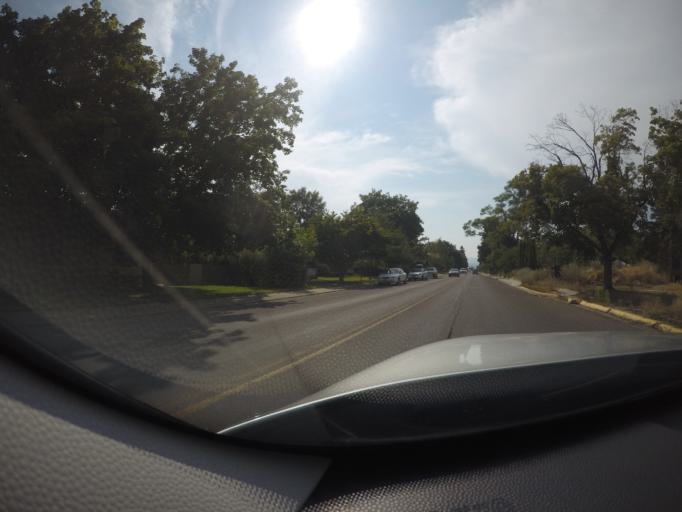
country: US
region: Montana
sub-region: Missoula County
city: Missoula
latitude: 46.8560
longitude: -114.0028
